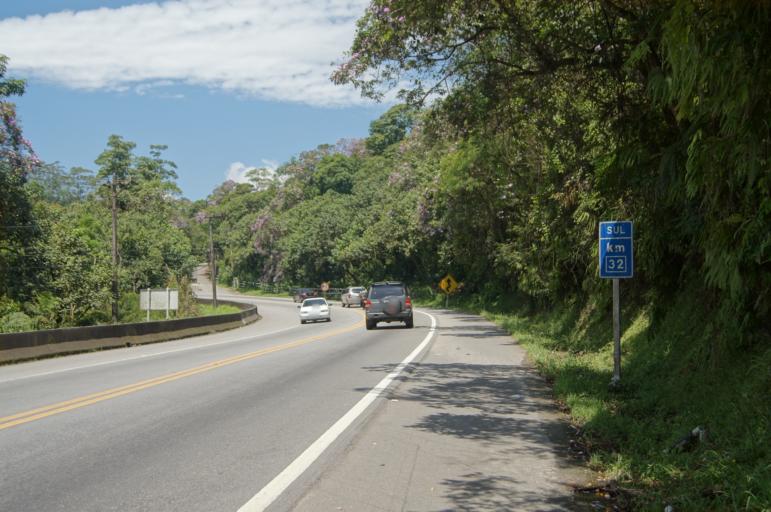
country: BR
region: Sao Paulo
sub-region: Sao Bernardo Do Campo
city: Sao Bernardo do Campo
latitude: -23.7845
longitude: -46.5078
